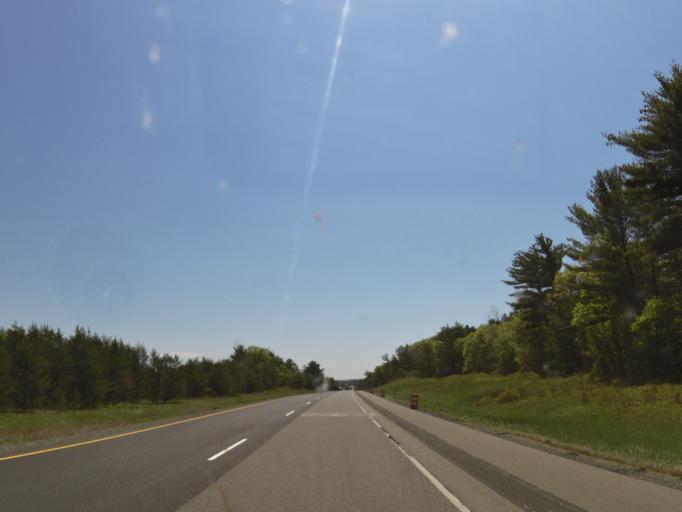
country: US
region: Wisconsin
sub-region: Jackson County
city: Black River Falls
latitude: 44.2100
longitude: -90.6697
